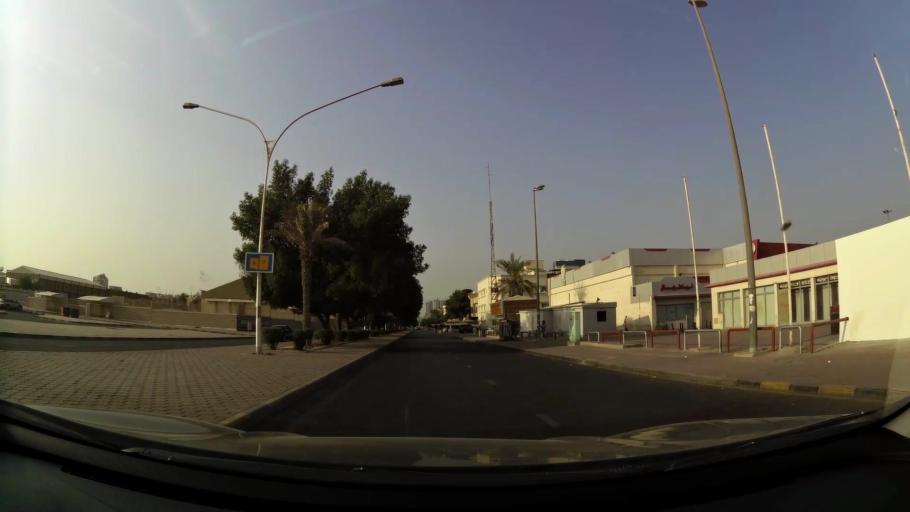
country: KW
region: Muhafazat Hawalli
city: Hawalli
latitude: 29.3171
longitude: 48.0340
